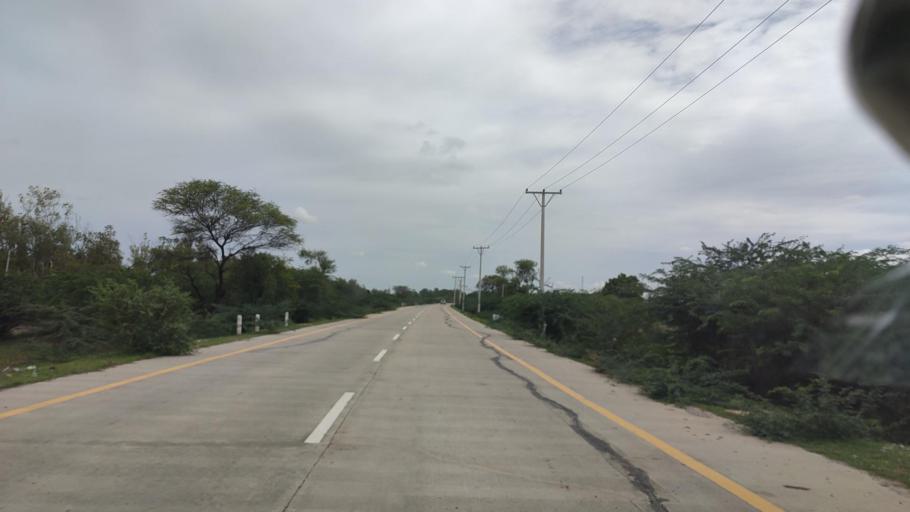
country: MM
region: Mandalay
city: Meiktila
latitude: 21.1323
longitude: 96.0277
